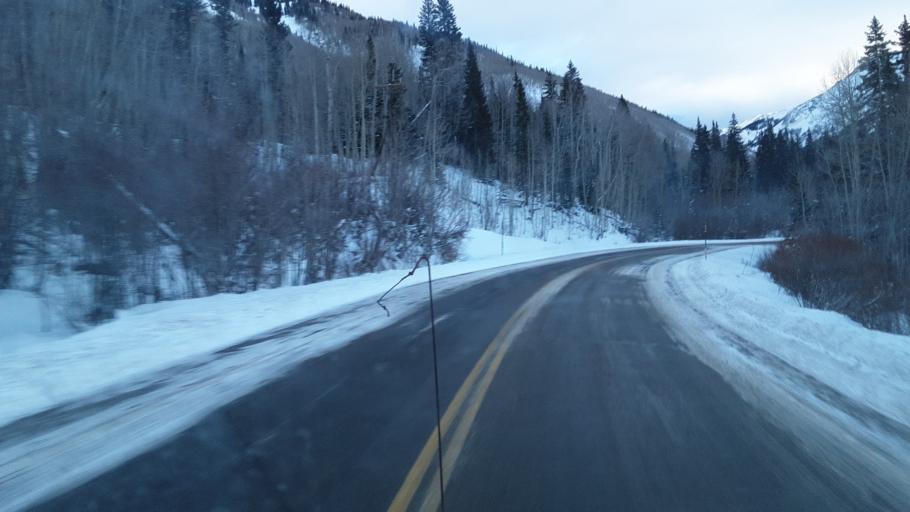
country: US
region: Colorado
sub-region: Ouray County
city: Ouray
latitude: 37.9280
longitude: -107.6904
